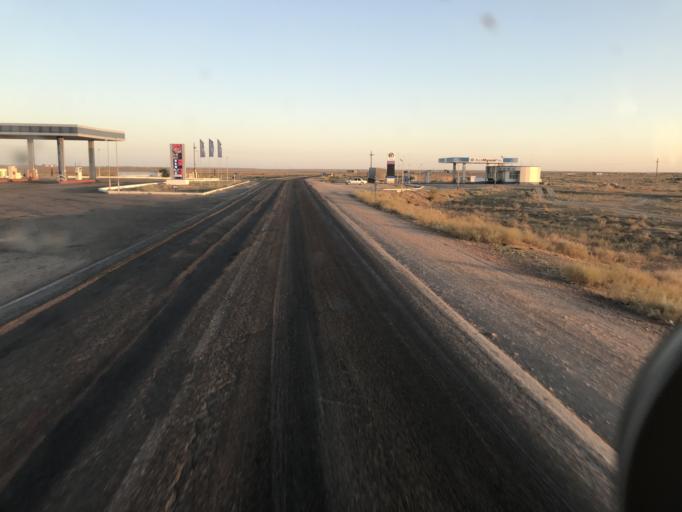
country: KZ
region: Qaraghandy
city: Saryshaghan
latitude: 46.0207
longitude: 73.5915
